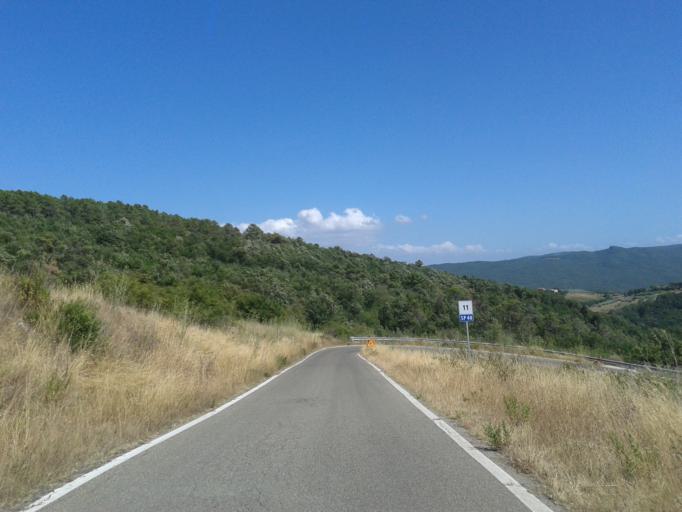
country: IT
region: Tuscany
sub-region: Province of Pisa
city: Chianni
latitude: 43.4633
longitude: 10.6317
